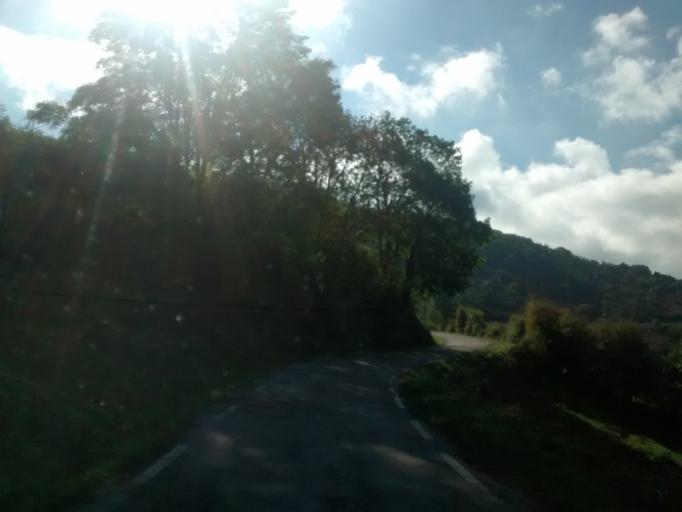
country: ES
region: Castille and Leon
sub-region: Provincia de Burgos
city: Arija
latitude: 42.9344
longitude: -4.0297
